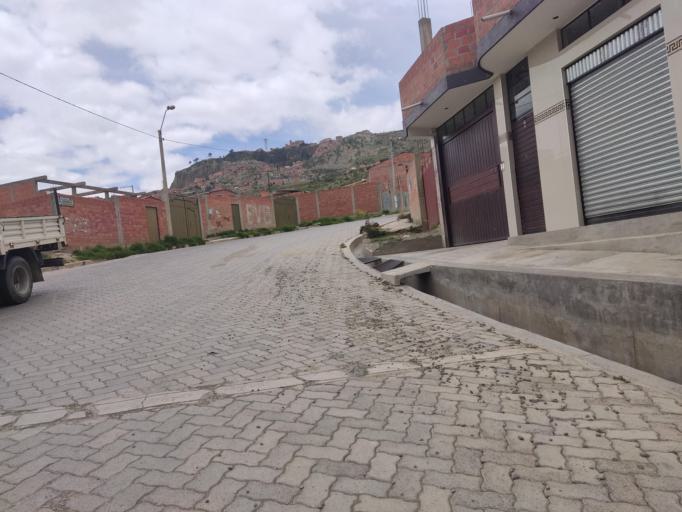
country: BO
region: La Paz
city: La Paz
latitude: -16.5014
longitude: -68.0929
